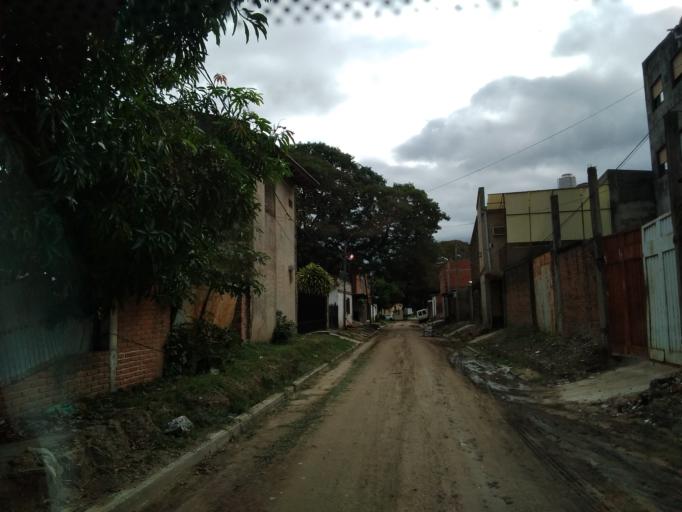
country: AR
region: Corrientes
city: Corrientes
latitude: -27.4726
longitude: -58.8085
